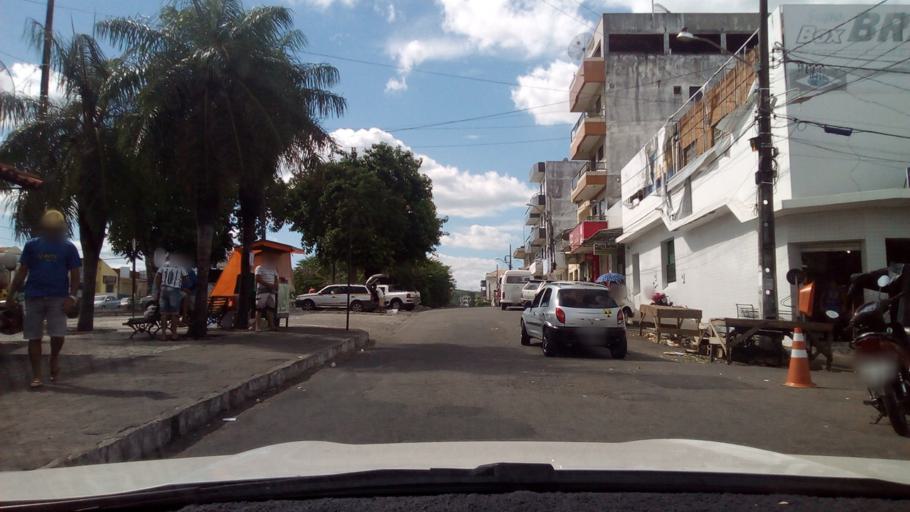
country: BR
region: Paraiba
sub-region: Guarabira
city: Guarabira
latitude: -6.8508
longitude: -35.4927
